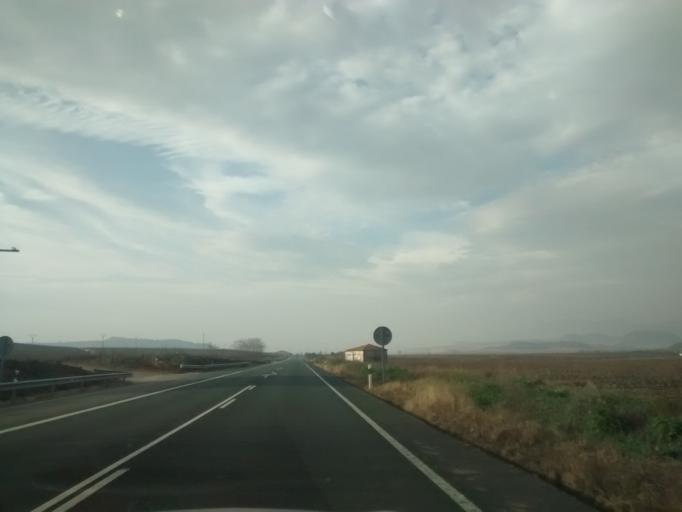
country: ES
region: La Rioja
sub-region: Provincia de La Rioja
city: Torremontalbo
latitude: 42.4913
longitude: -2.6642
